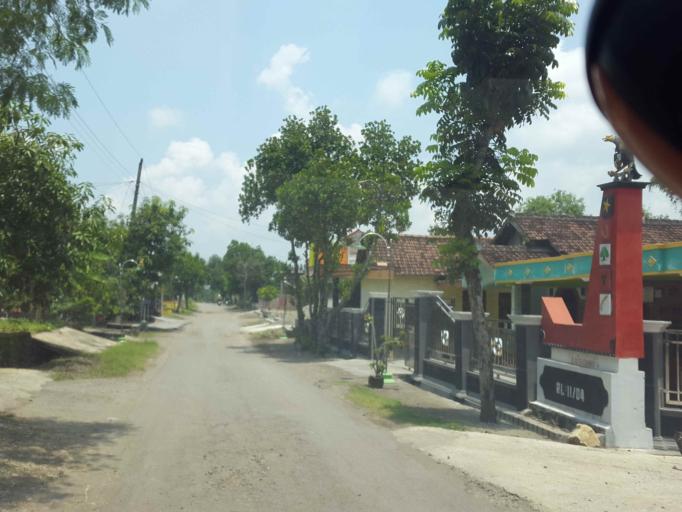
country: ID
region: Central Java
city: Sragen
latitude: -7.4110
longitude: 110.9810
